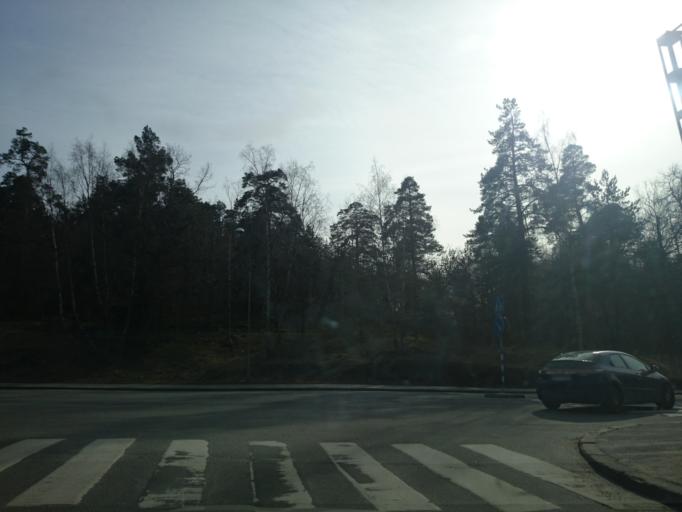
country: SE
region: Stockholm
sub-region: Nacka Kommun
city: Alta
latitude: 59.2412
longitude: 18.1111
